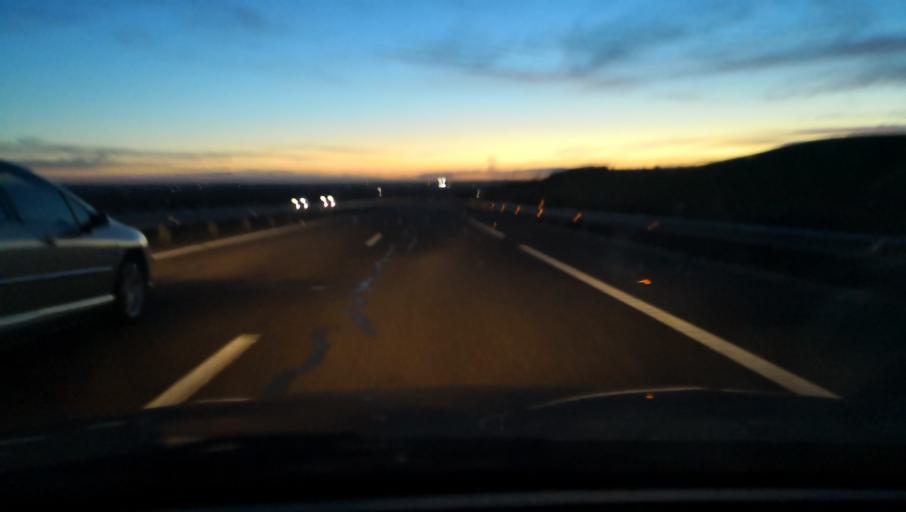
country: ES
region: Castille and Leon
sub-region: Provincia de Zamora
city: Coreses
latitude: 41.5490
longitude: -5.6460
